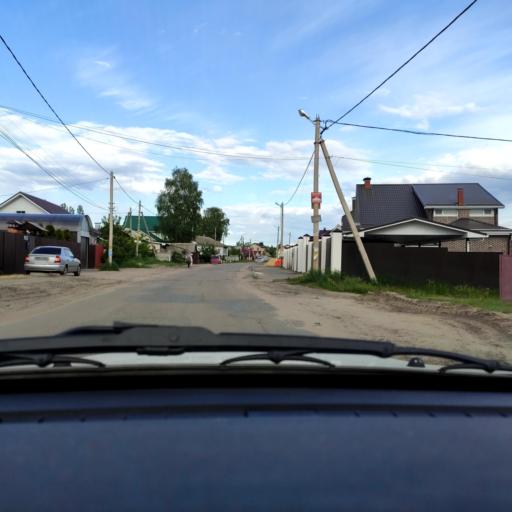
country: RU
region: Voronezj
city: Podgornoye
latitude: 51.7403
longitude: 39.1524
